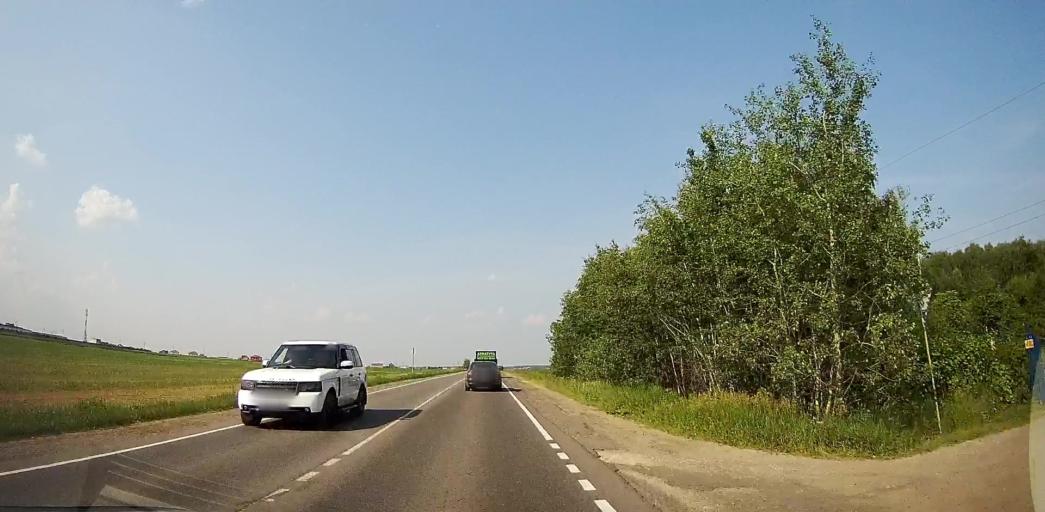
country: RU
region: Moskovskaya
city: Zhitnevo
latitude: 55.3314
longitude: 37.9039
